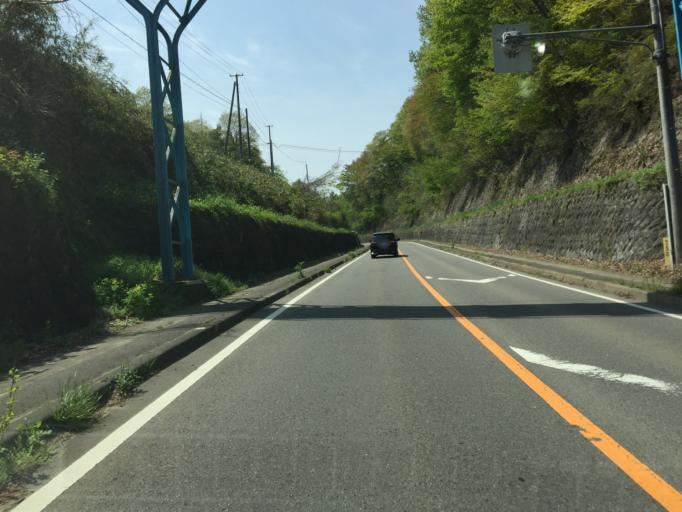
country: JP
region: Fukushima
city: Nihommatsu
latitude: 37.6446
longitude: 140.4637
